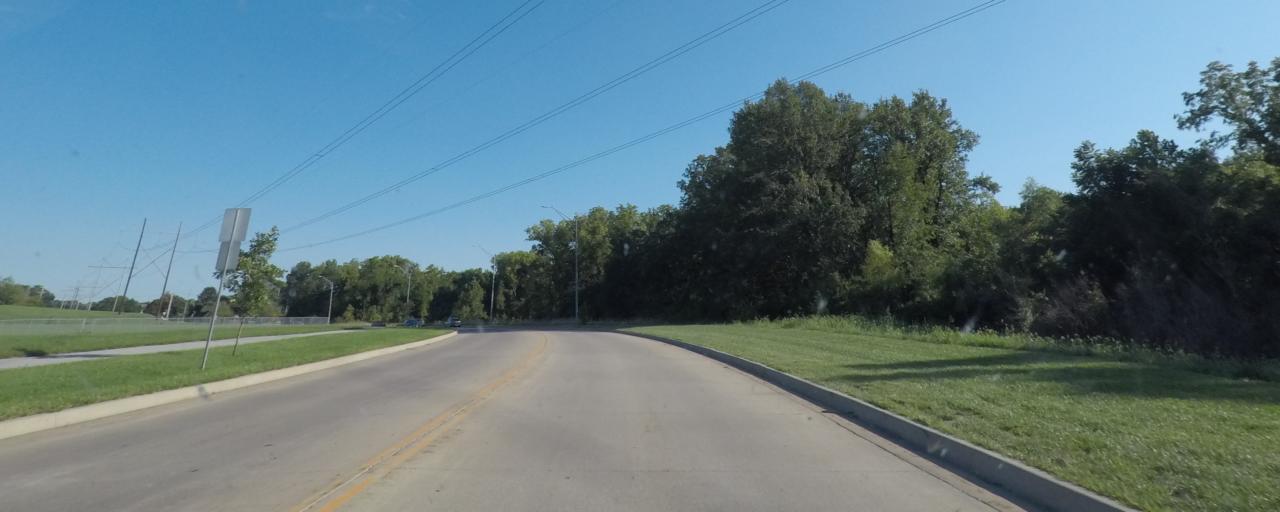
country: US
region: Missouri
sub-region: Clay County
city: Pleasant Valley
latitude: 39.2247
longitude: -94.4656
